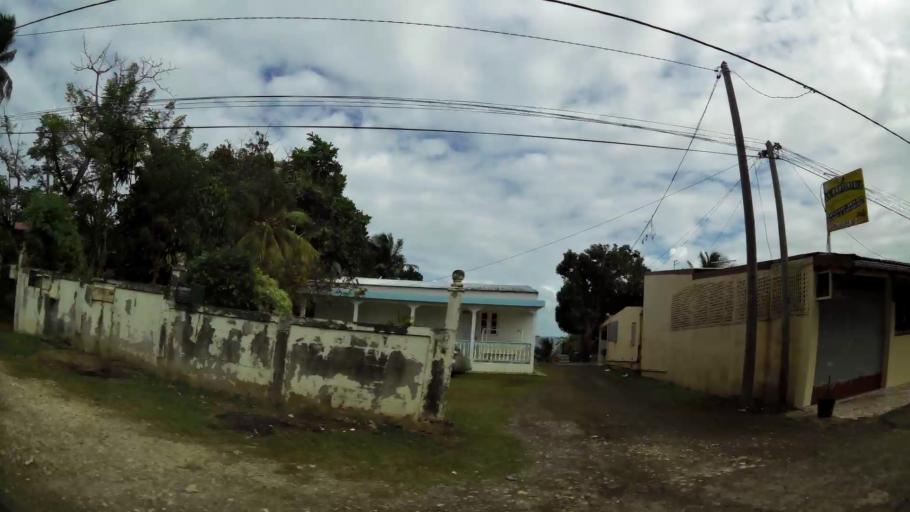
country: GP
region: Guadeloupe
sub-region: Guadeloupe
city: Sainte-Rose
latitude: 16.3401
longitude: -61.7171
